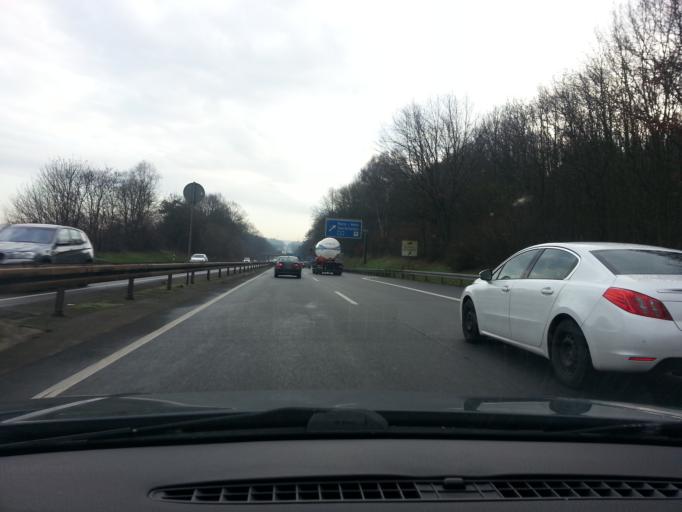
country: DE
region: Saarland
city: Kirkel
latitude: 49.3116
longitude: 7.2479
